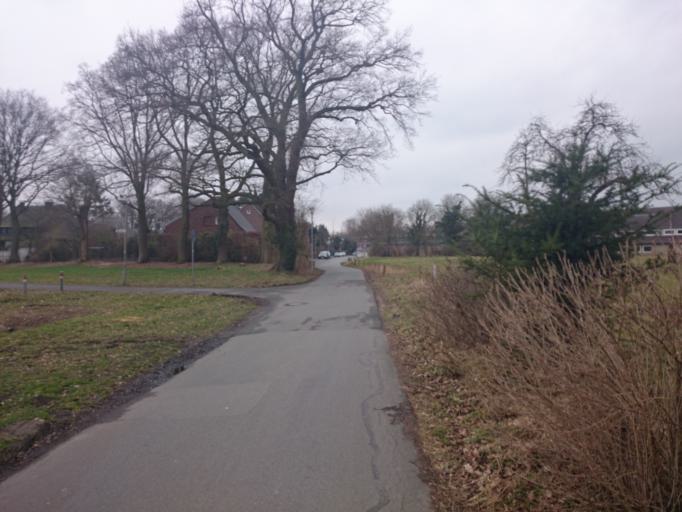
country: DE
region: North Rhine-Westphalia
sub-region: Regierungsbezirk Munster
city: Muenster
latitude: 51.9329
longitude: 7.5824
